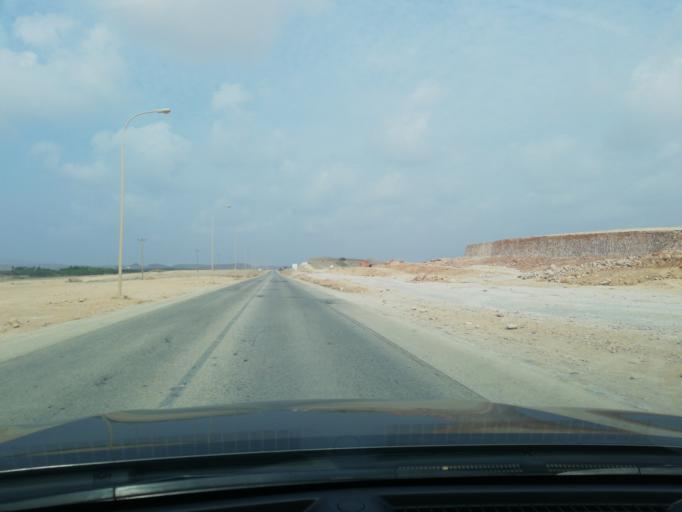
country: OM
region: Zufar
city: Salalah
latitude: 16.9466
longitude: 53.9571
